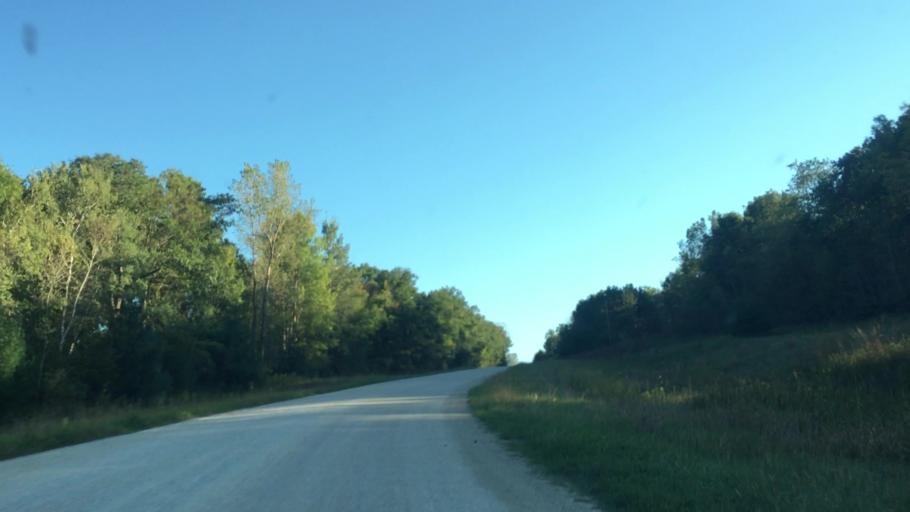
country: US
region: Minnesota
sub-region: Fillmore County
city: Preston
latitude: 43.7816
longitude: -92.0294
